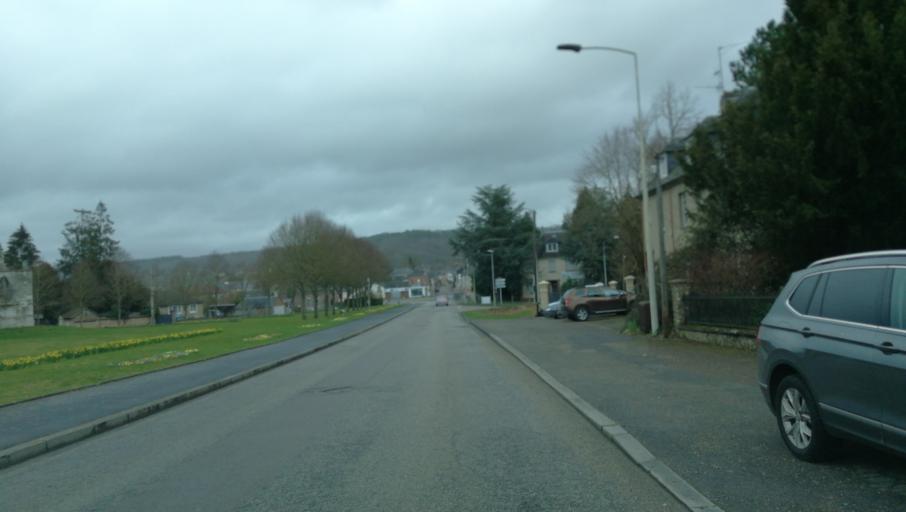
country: FR
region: Haute-Normandie
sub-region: Departement de l'Eure
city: Brionne
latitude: 49.1924
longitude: 0.7122
